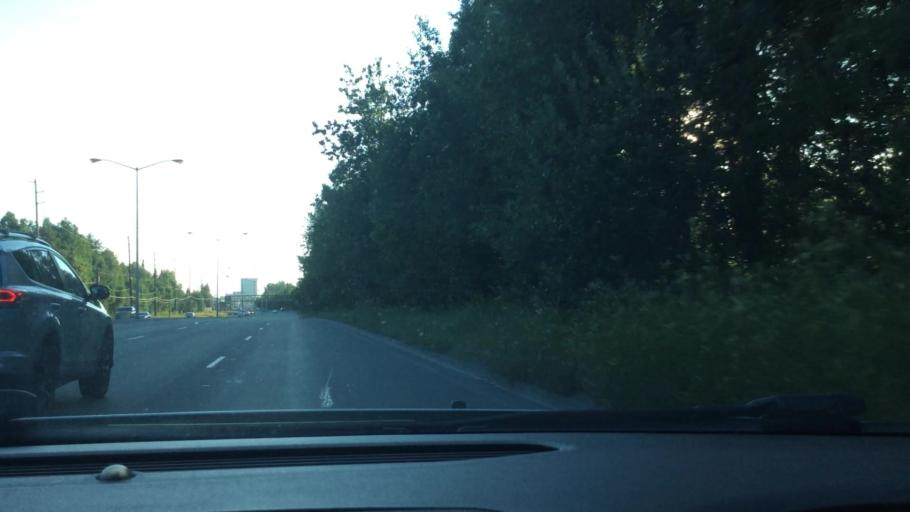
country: US
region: Alaska
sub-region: Anchorage Municipality
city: Anchorage
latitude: 61.1955
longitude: -149.8474
